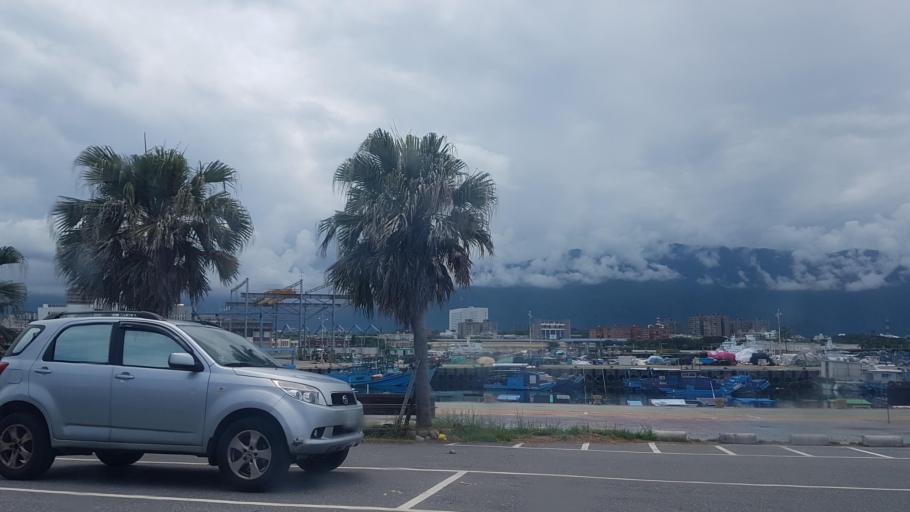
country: TW
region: Taiwan
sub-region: Hualien
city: Hualian
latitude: 23.9970
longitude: 121.6405
